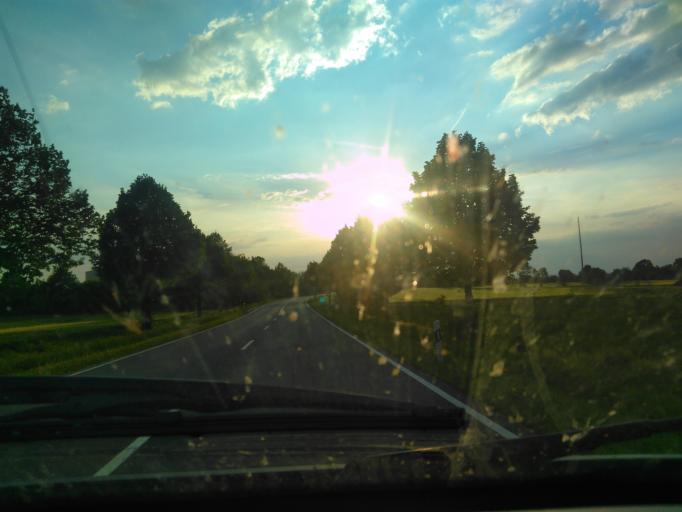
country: DE
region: Saxony-Anhalt
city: Stossen
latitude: 51.1119
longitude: 11.9129
